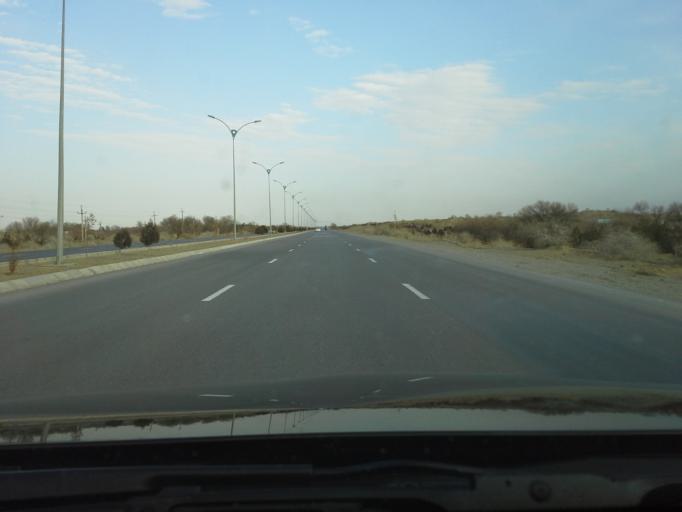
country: TM
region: Ahal
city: Abadan
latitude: 38.1031
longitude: 58.3188
